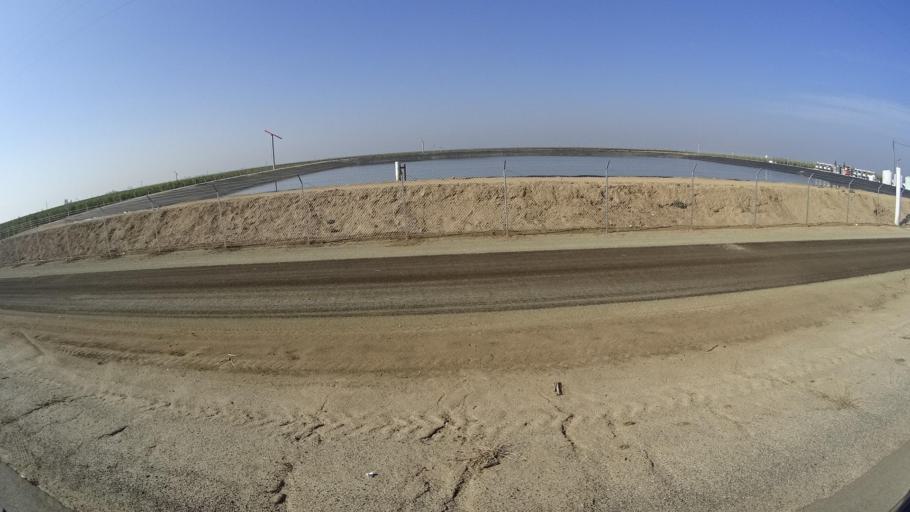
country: US
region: California
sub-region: Kern County
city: McFarland
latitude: 35.6233
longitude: -119.1687
